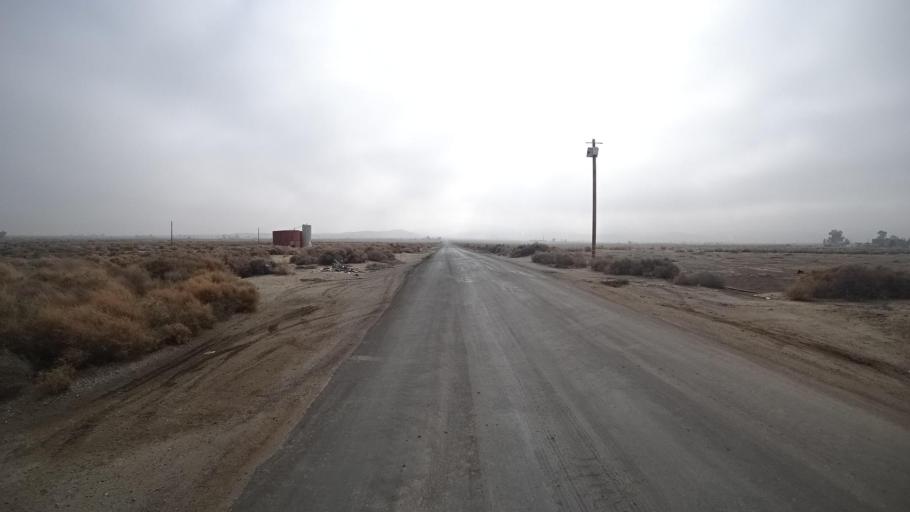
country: US
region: California
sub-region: Kern County
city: Maricopa
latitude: 35.0577
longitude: -119.3670
